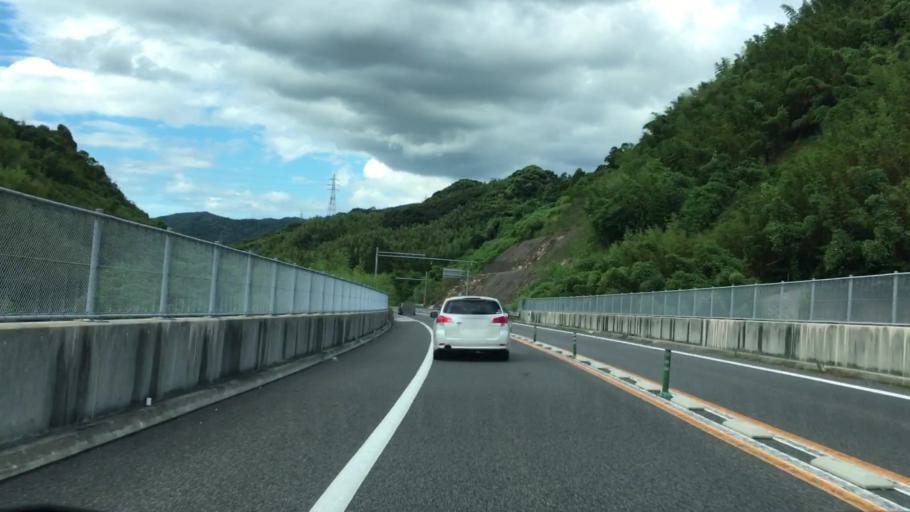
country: JP
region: Saga Prefecture
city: Karatsu
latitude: 33.4304
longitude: 130.0479
